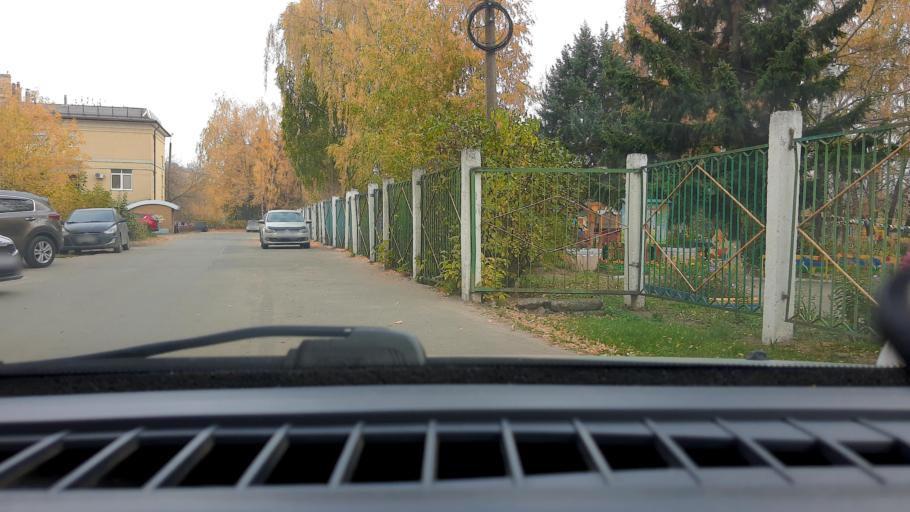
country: RU
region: Nizjnij Novgorod
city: Gorbatovka
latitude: 56.3297
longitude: 43.8411
